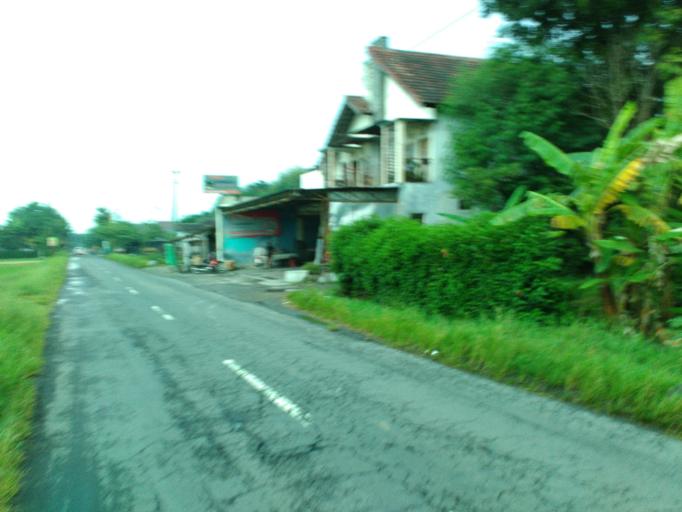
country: ID
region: Central Java
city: Ceper
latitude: -7.6514
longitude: 110.6859
